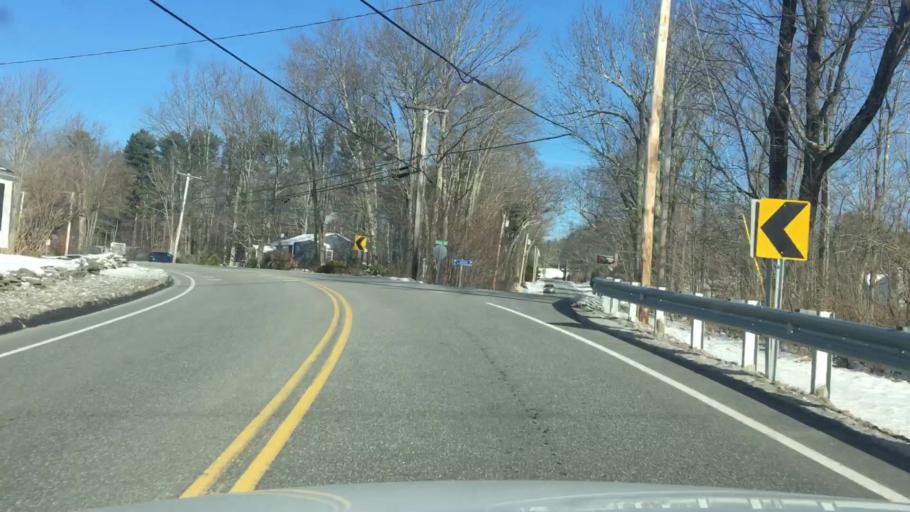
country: US
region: Maine
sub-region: Cumberland County
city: Freeport
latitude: 43.8815
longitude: -70.0930
